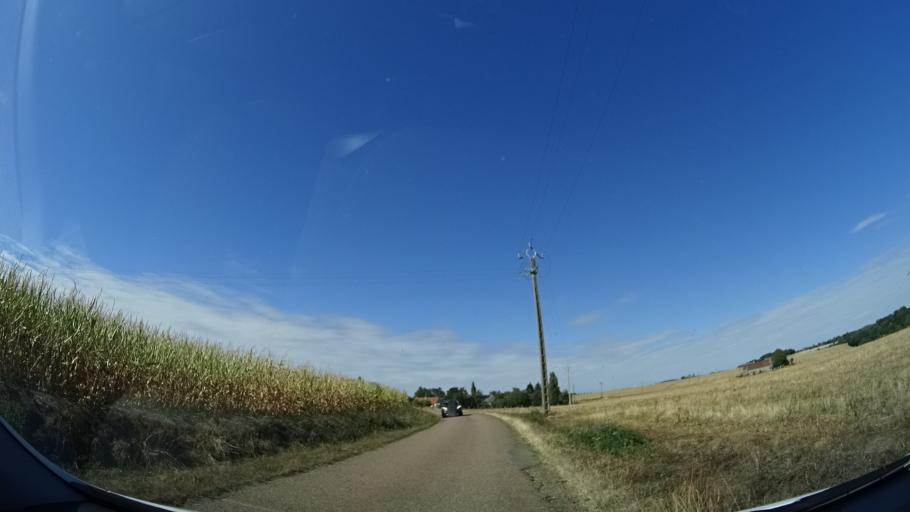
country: FR
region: Centre
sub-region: Departement du Loiret
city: Trigueres
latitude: 47.9561
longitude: 2.9796
